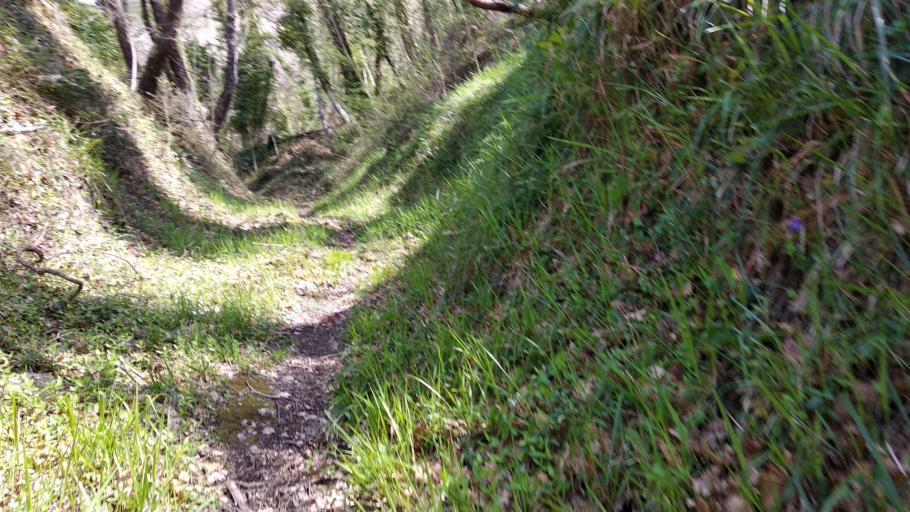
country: IT
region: Calabria
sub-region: Provincia di Cosenza
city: Altilia
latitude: 39.1274
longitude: 16.2485
